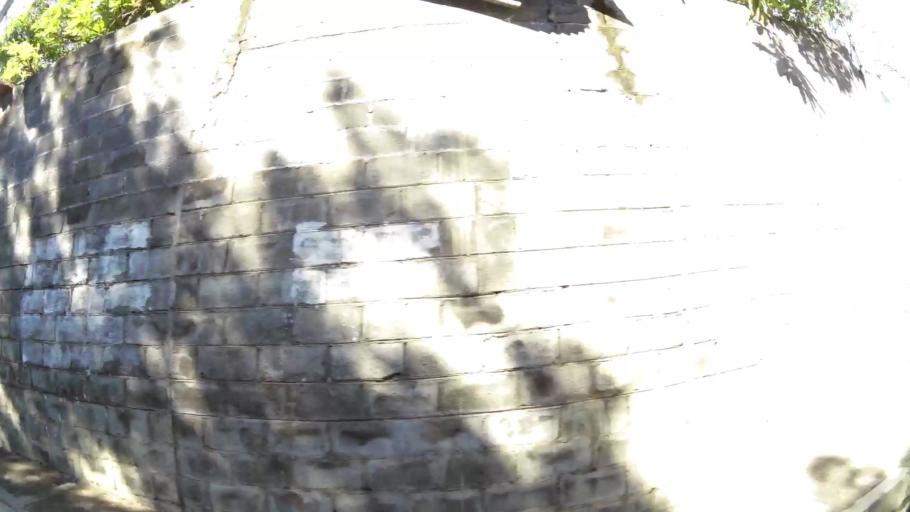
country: SV
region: San Miguel
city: San Miguel
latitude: 13.4620
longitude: -88.1608
